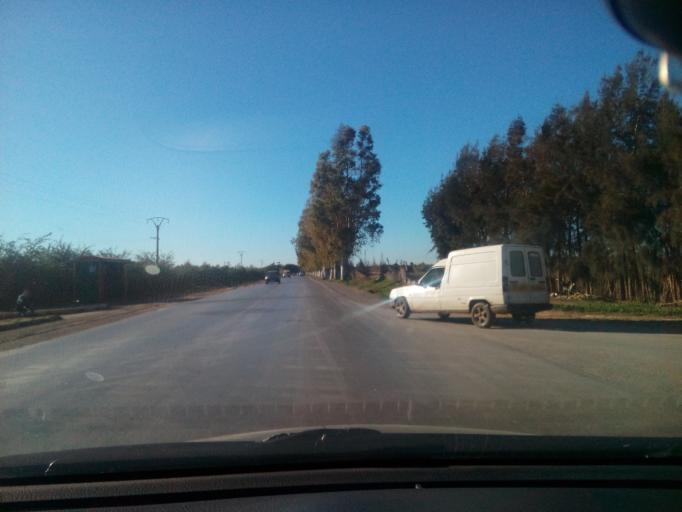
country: DZ
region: Mostaganem
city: Mostaganem
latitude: 35.9003
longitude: 0.2244
